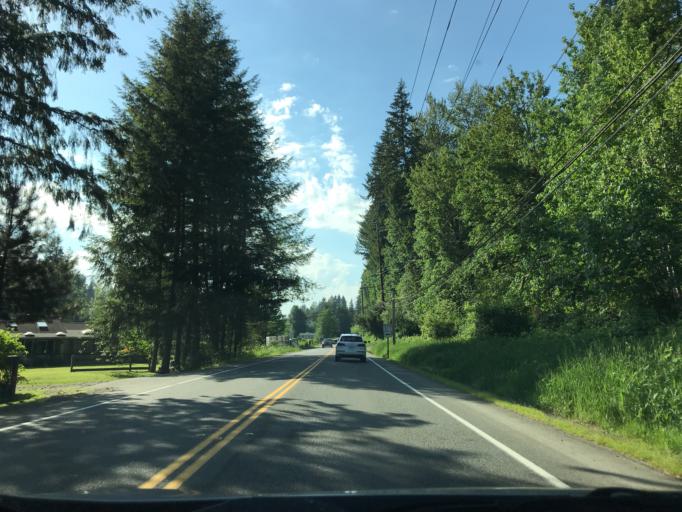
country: US
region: Washington
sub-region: King County
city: Mirrormont
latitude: 47.4580
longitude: -122.0032
